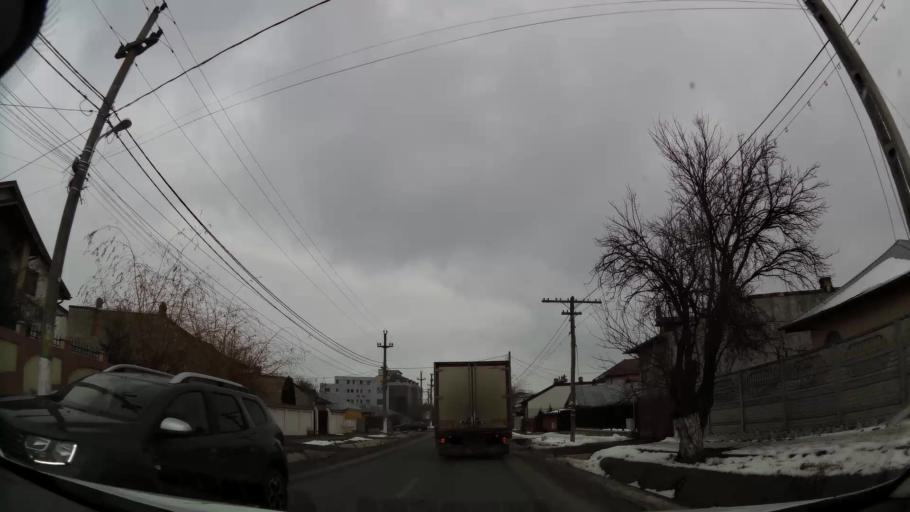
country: RO
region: Ilfov
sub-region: Comuna Afumati
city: Afumati
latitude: 44.5245
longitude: 26.2481
